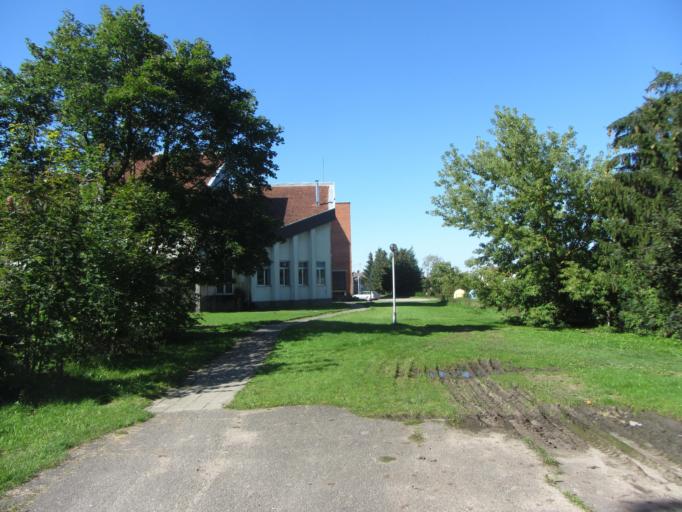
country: LT
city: Simnas
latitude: 54.4370
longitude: 23.7661
